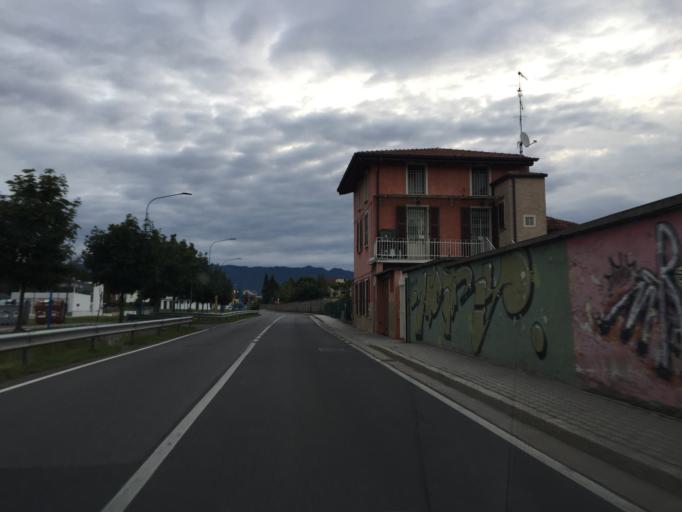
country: IT
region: Lombardy
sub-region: Provincia di Brescia
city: Brescia
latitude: 45.5211
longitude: 10.1979
